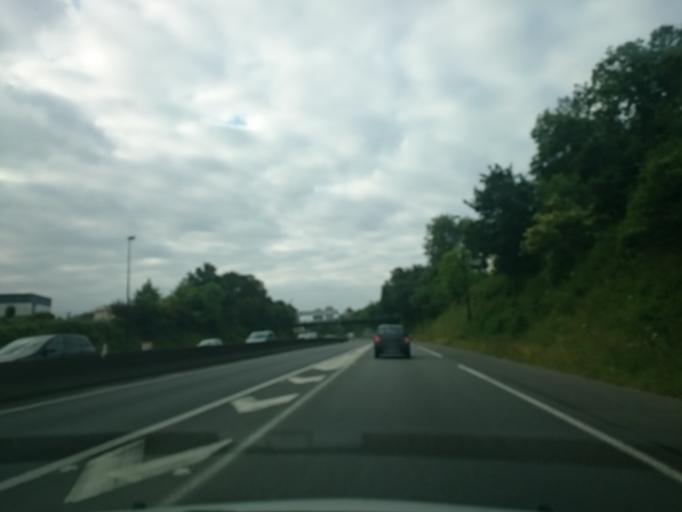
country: FR
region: Brittany
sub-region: Departement du Finistere
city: Le Relecq-Kerhuon
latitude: 48.3966
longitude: -4.4086
